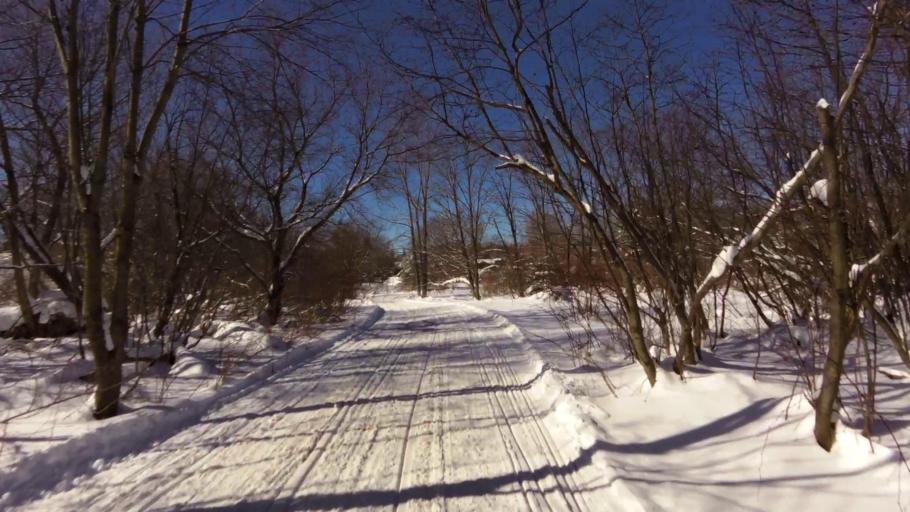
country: US
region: New York
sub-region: Chautauqua County
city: Mayville
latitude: 42.1578
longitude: -79.5923
